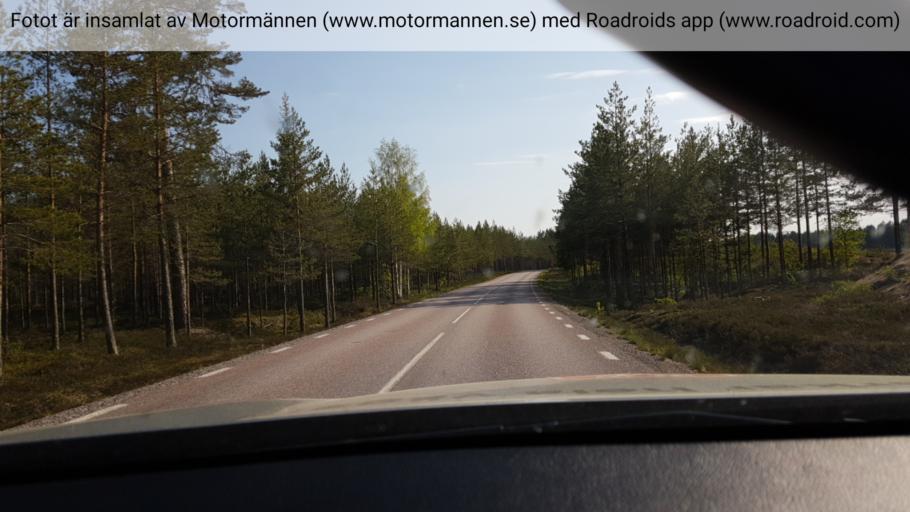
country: SE
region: Gaevleborg
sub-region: Sandvikens Kommun
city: Arsunda
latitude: 60.4717
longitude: 16.7099
